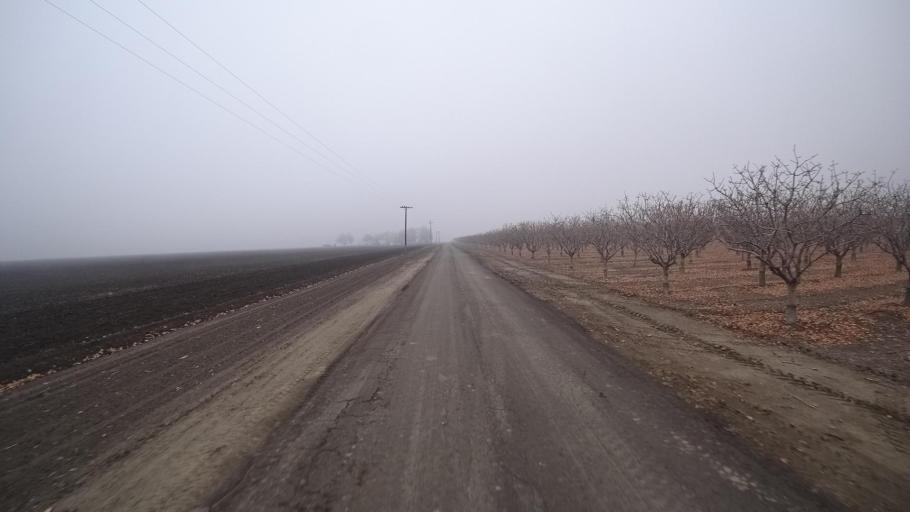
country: US
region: California
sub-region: Kern County
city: Buttonwillow
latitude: 35.4268
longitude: -119.5524
